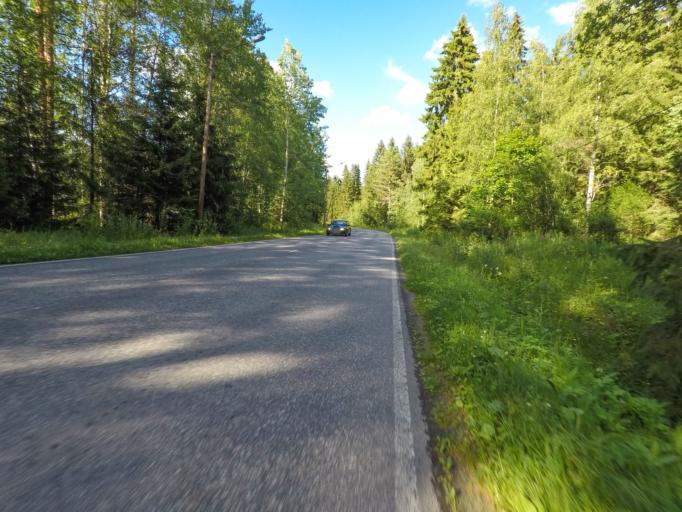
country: FI
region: South Karelia
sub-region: Imatra
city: Imatra
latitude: 61.1472
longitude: 28.7515
